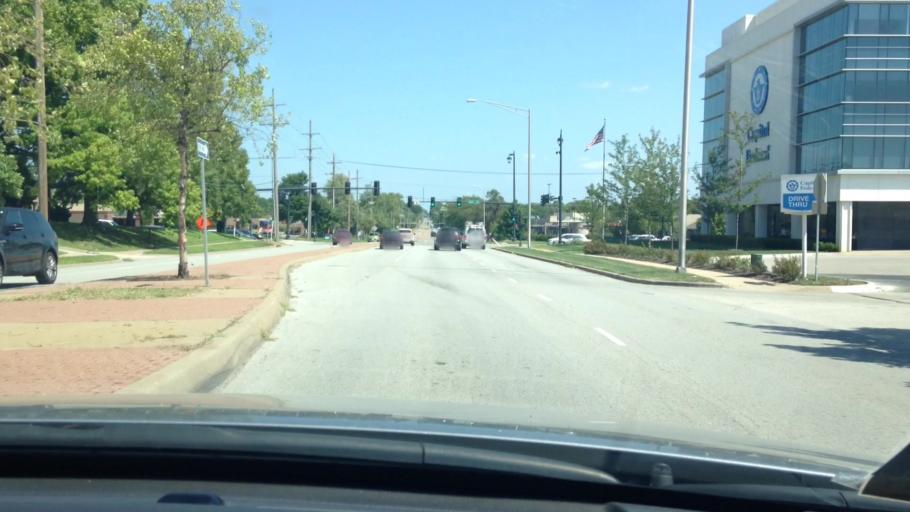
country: US
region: Kansas
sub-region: Johnson County
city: Overland Park
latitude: 38.9567
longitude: -94.6504
